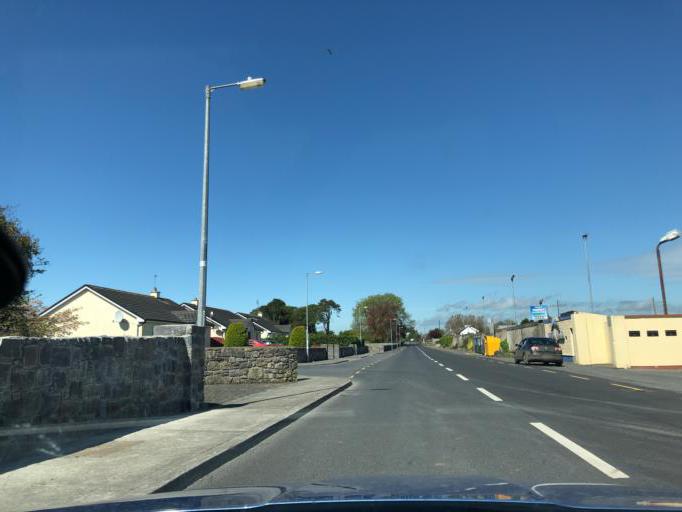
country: IE
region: Connaught
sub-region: County Galway
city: Portumna
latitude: 53.1524
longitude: -8.3770
